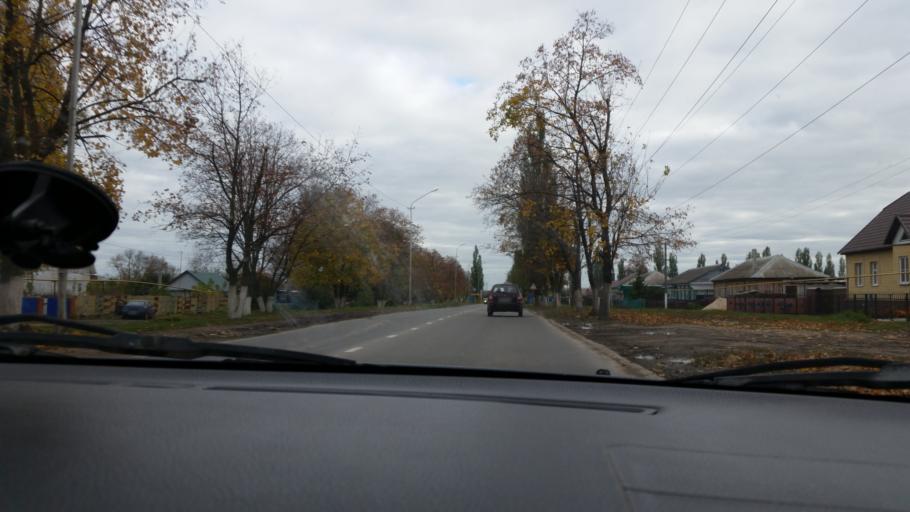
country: RU
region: Lipetsk
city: Gryazi
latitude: 52.4825
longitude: 39.9488
